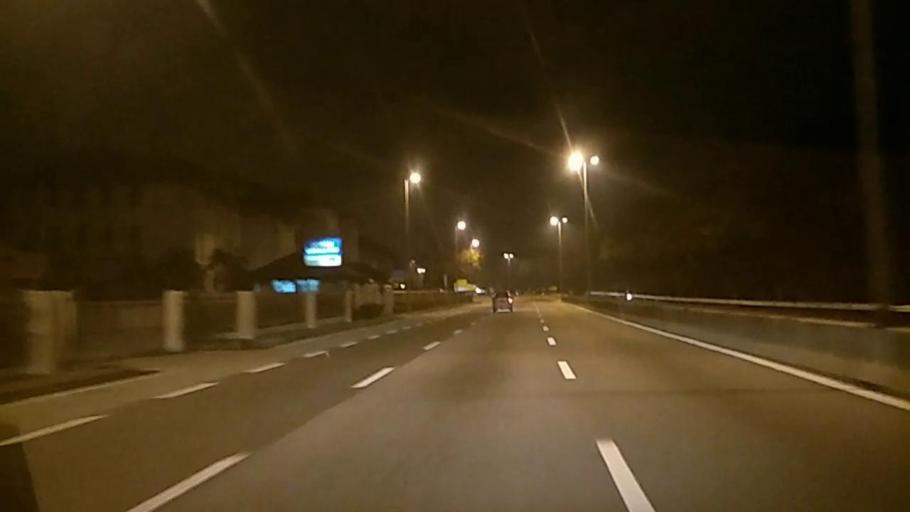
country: MY
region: Selangor
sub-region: Petaling
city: Petaling Jaya
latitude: 3.1009
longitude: 101.5975
